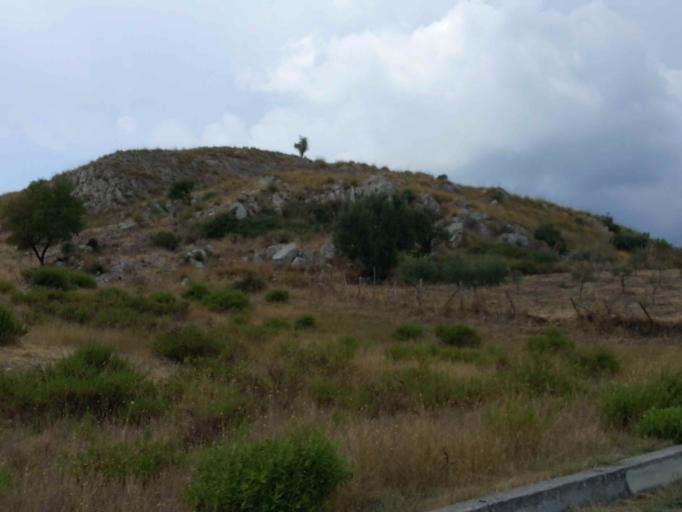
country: IT
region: Calabria
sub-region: Provincia di Reggio Calabria
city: San Lorenzo
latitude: 37.9812
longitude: 15.8347
